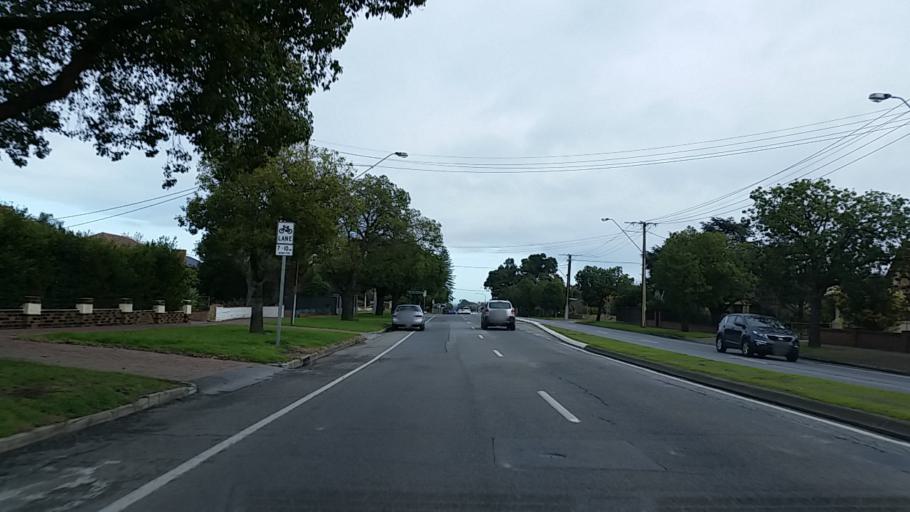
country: AU
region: South Australia
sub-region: Burnside
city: Tusmore
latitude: -34.9390
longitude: 138.6464
